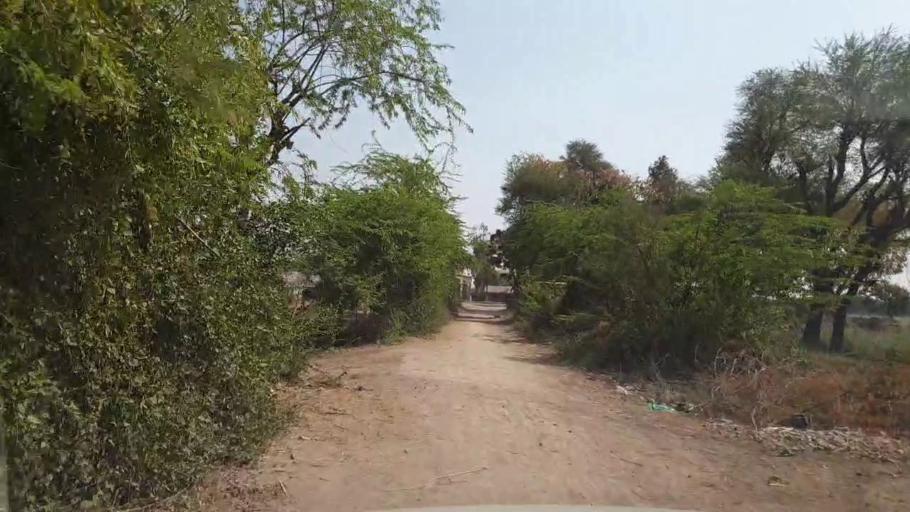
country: PK
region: Sindh
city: Dhoro Naro
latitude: 25.4564
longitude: 69.6314
